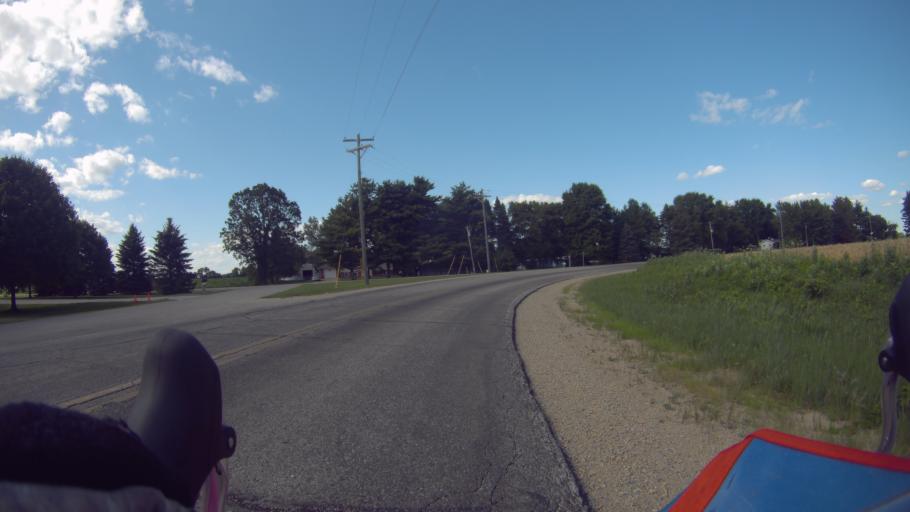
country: US
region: Wisconsin
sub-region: Dane County
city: Stoughton
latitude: 42.8957
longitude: -89.2548
